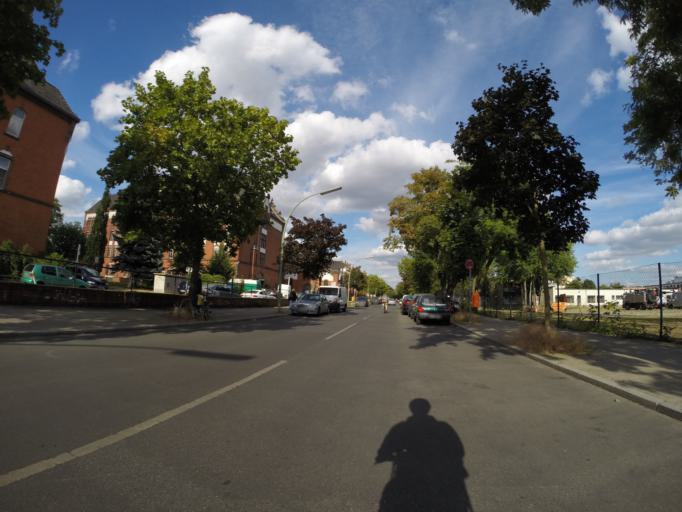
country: DE
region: Berlin
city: Schoneberg Bezirk
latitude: 52.4746
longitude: 13.3672
